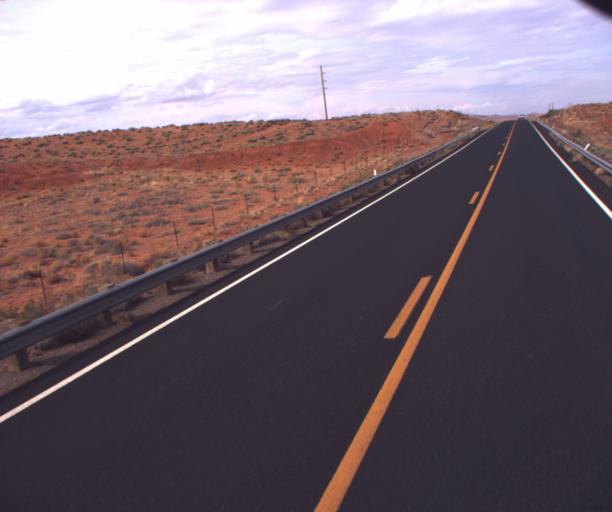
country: US
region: Arizona
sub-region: Apache County
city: Many Farms
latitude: 36.6030
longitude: -109.5712
